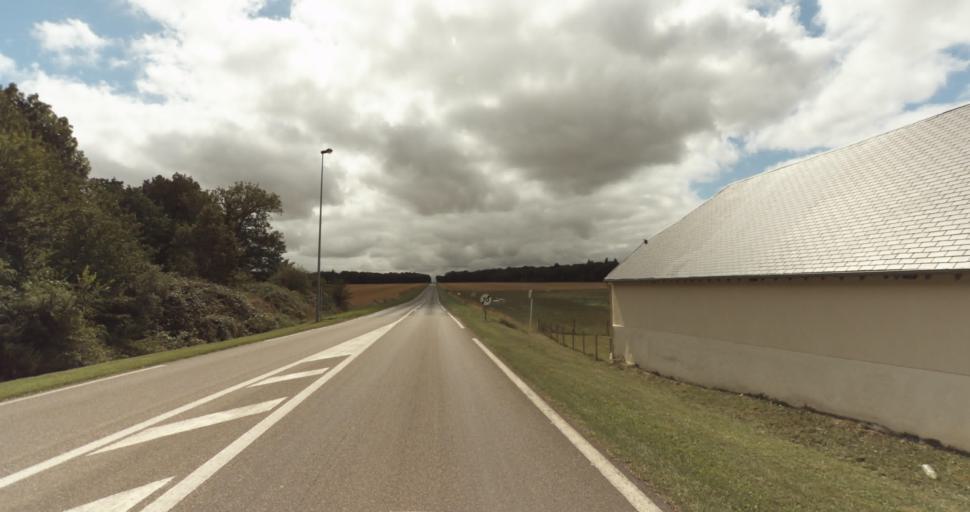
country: FR
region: Haute-Normandie
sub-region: Departement de l'Eure
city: Evreux
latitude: 48.9706
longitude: 1.1595
